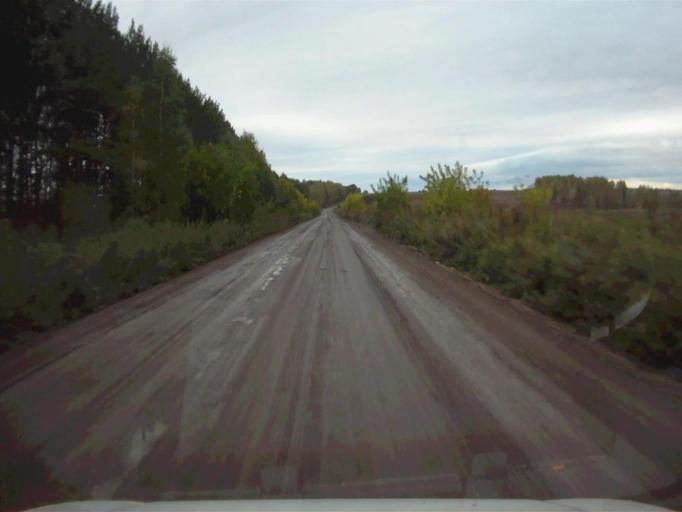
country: RU
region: Sverdlovsk
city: Mikhaylovsk
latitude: 56.1482
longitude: 59.2755
